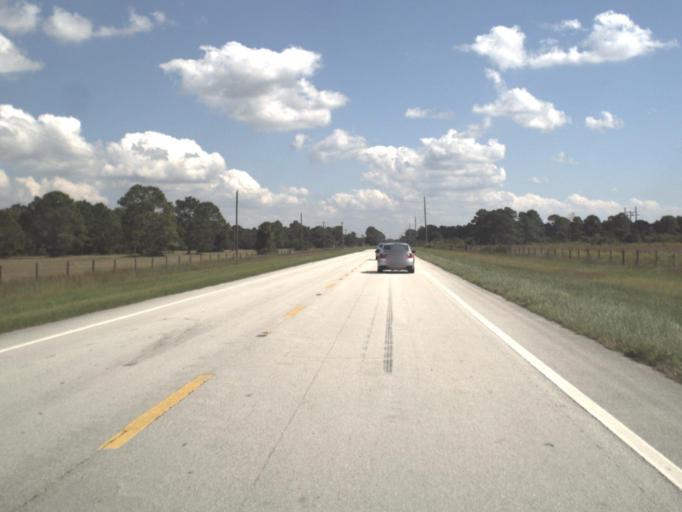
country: US
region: Florida
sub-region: Okeechobee County
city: Okeechobee
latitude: 27.3684
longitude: -81.0737
